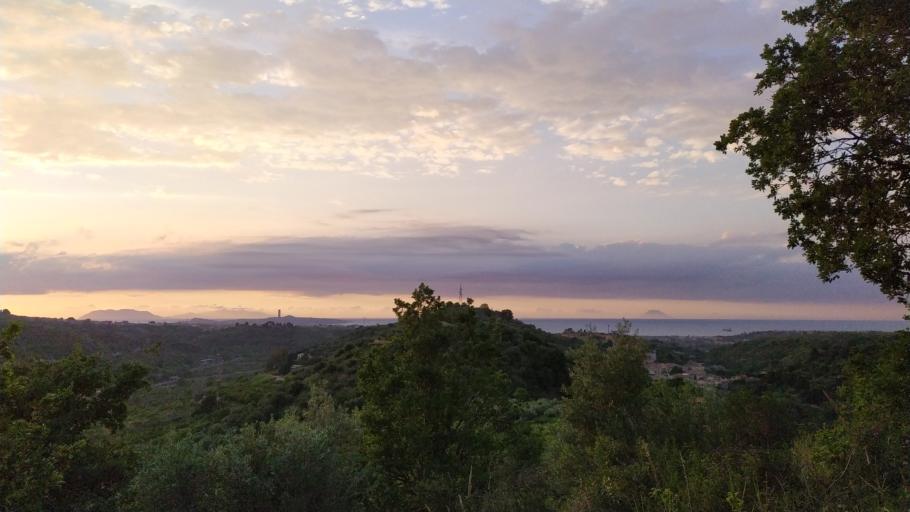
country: IT
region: Sicily
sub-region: Messina
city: Condro
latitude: 38.1639
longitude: 15.3281
